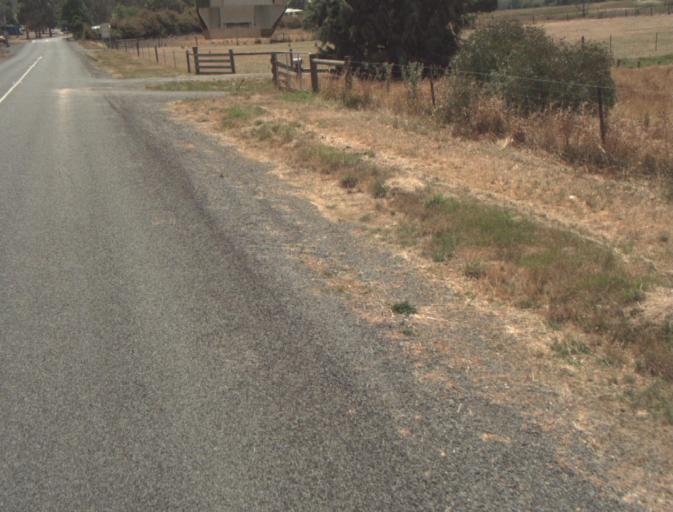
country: AU
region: Tasmania
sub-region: Launceston
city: Newstead
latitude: -41.4679
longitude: 147.1865
